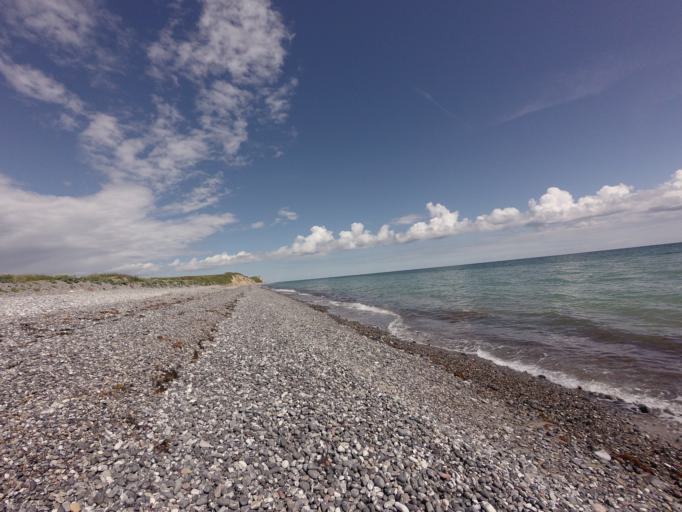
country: DK
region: Central Jutland
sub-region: Norddjurs Kommune
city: Grenaa
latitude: 56.5003
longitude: 10.8691
